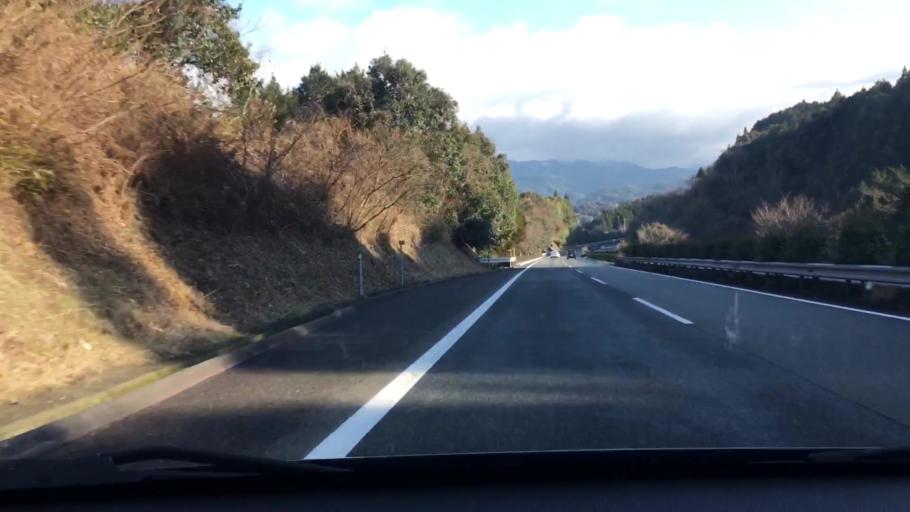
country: JP
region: Kumamoto
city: Hitoyoshi
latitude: 32.1813
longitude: 130.7831
